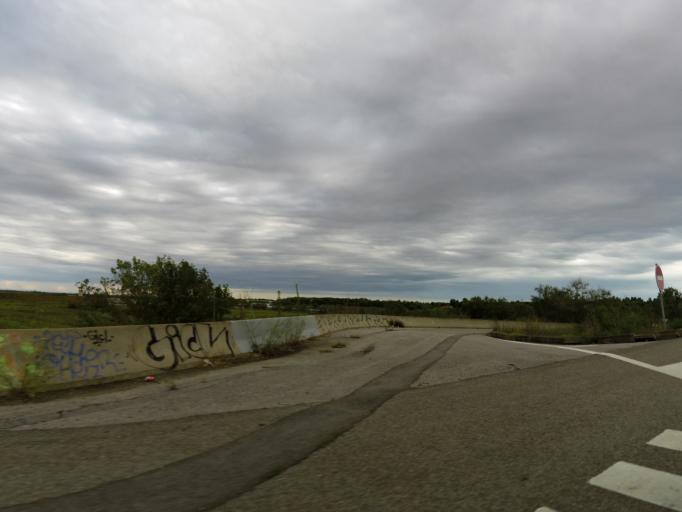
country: FR
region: Languedoc-Roussillon
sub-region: Departement du Gard
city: Aigues-Mortes
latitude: 43.5900
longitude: 4.1961
